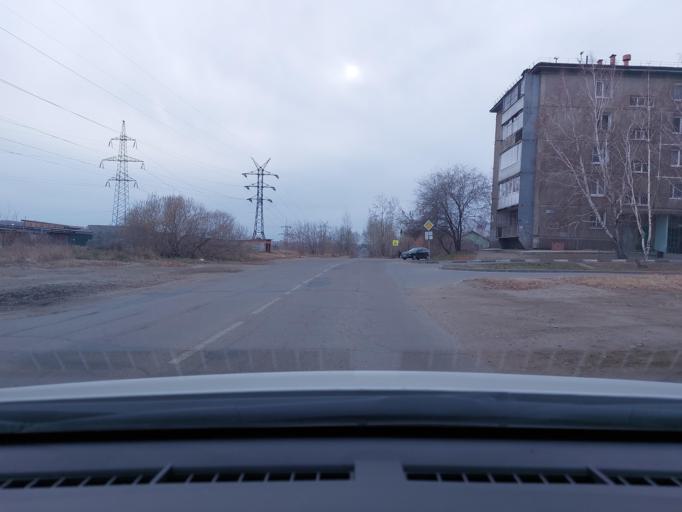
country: RU
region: Irkutsk
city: Smolenshchina
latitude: 52.3462
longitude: 104.1652
